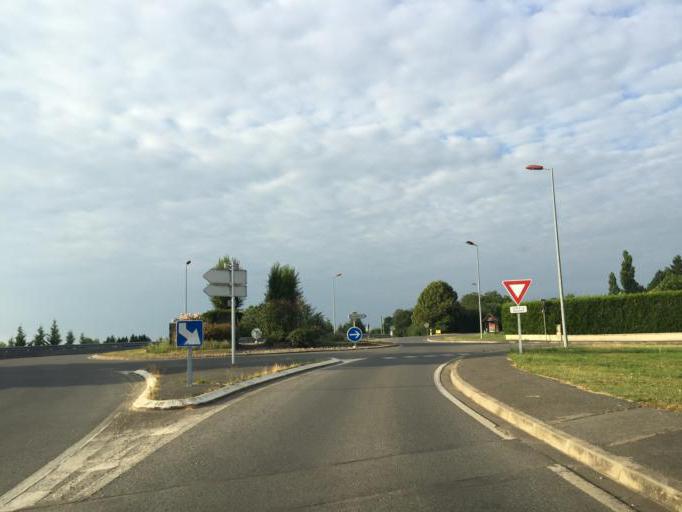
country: FR
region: Auvergne
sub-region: Departement de l'Allier
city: Saint-Remy-en-Rollat
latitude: 46.1816
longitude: 3.4190
